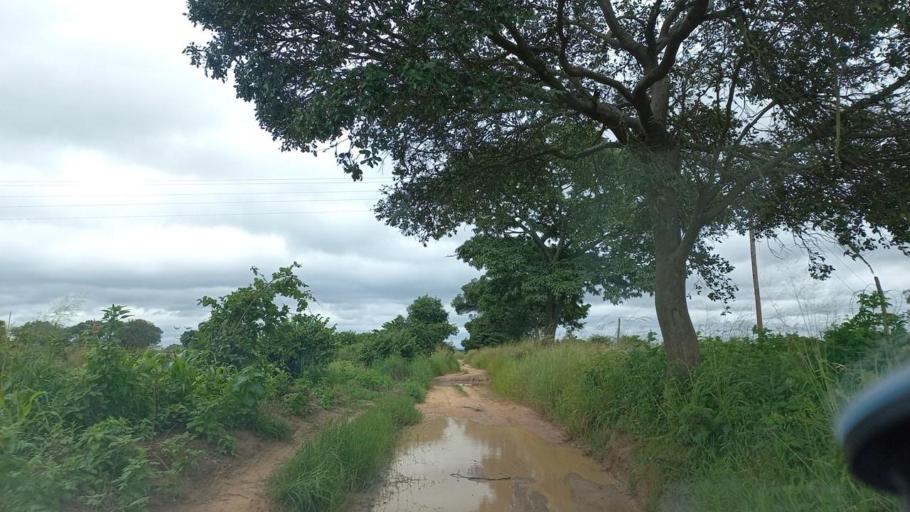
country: ZM
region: Lusaka
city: Lusaka
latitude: -15.1193
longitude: 28.3724
